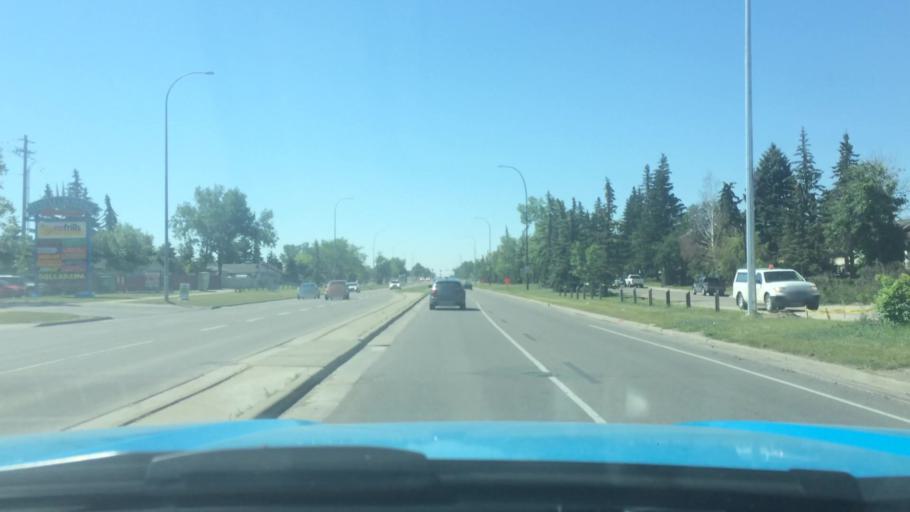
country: CA
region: Alberta
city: Calgary
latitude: 51.0855
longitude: -113.9585
